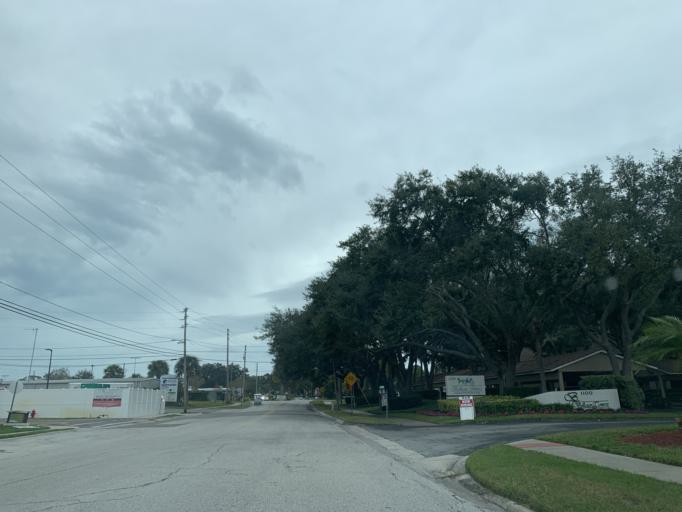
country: US
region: Florida
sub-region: Pinellas County
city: Belleair
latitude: 27.9352
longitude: -82.7993
